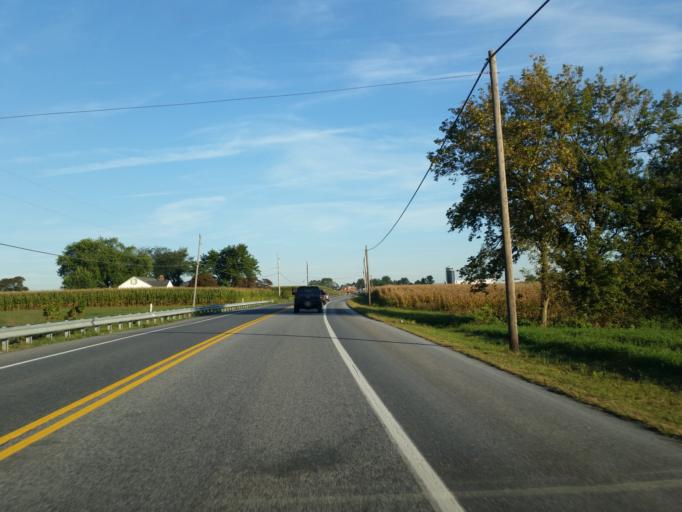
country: US
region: Pennsylvania
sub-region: Lancaster County
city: Quarryville
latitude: 39.8264
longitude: -76.2069
